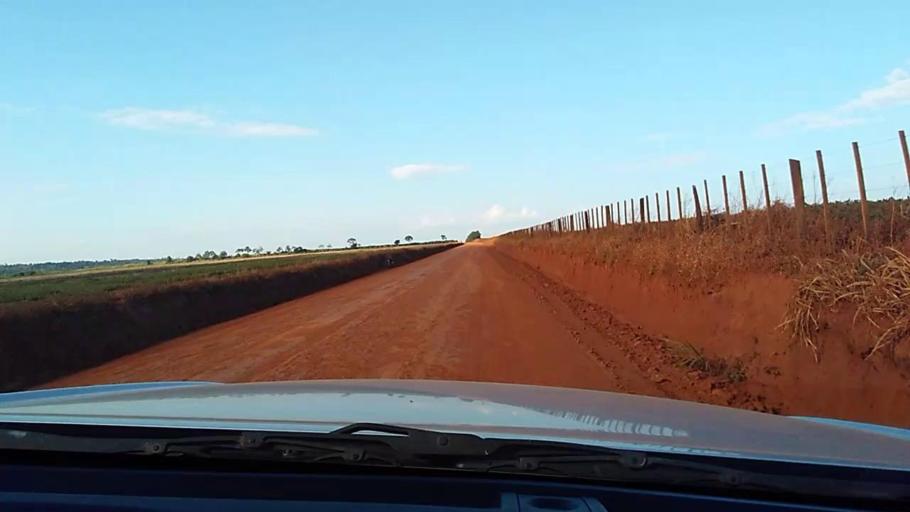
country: PY
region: Alto Parana
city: Naranjal
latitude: -25.7095
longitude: -55.3905
